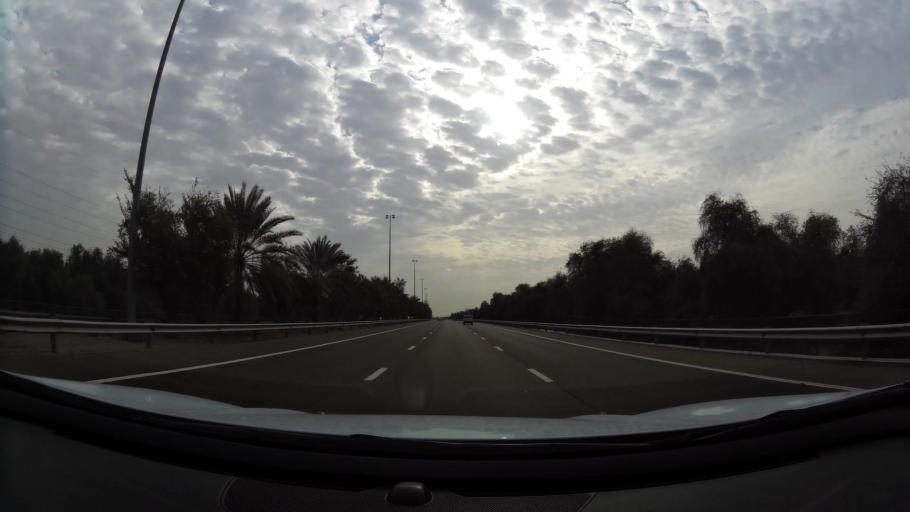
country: AE
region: Abu Dhabi
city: Al Ain
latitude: 24.1755
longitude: 55.2006
